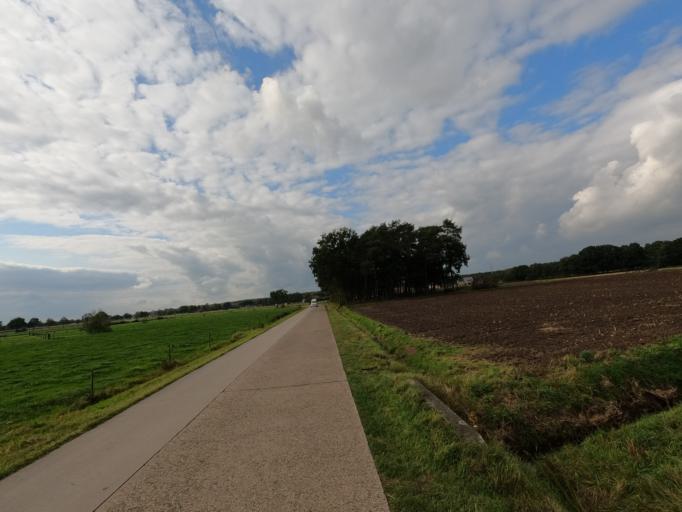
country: BE
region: Flanders
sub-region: Provincie Antwerpen
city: Kasterlee
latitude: 51.2212
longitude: 4.9573
